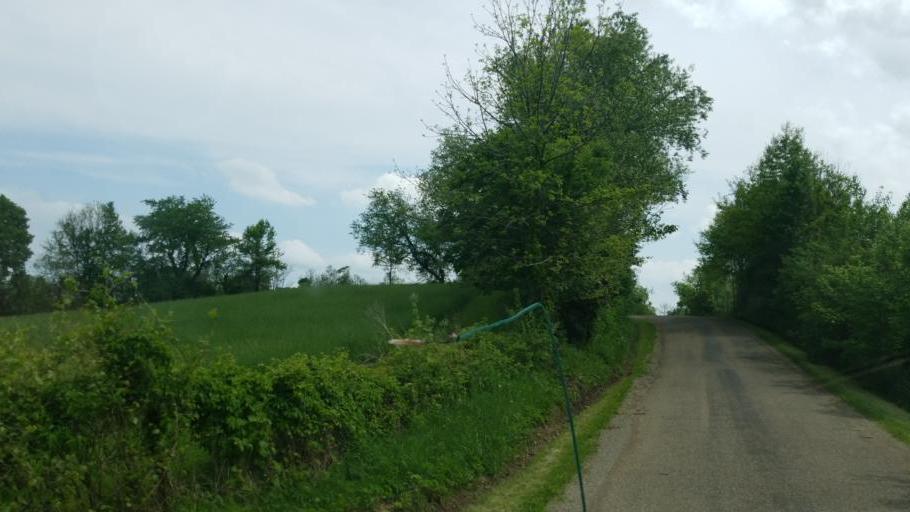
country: US
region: Ohio
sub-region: Ashland County
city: Ashland
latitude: 40.8088
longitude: -82.3867
